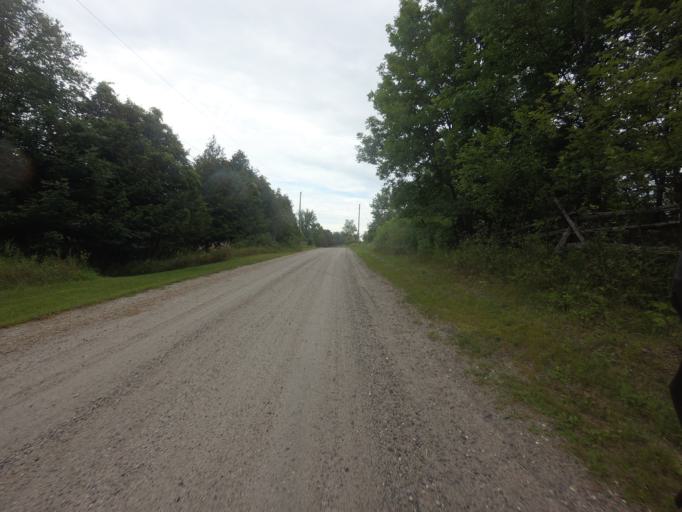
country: CA
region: Ontario
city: Perth
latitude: 45.0516
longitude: -76.3941
